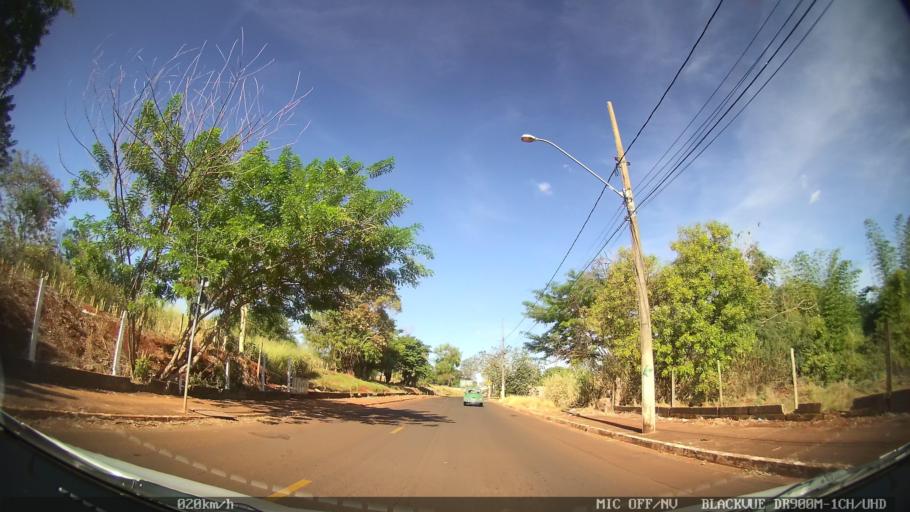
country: BR
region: Sao Paulo
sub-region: Ribeirao Preto
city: Ribeirao Preto
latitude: -21.1702
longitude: -47.7858
